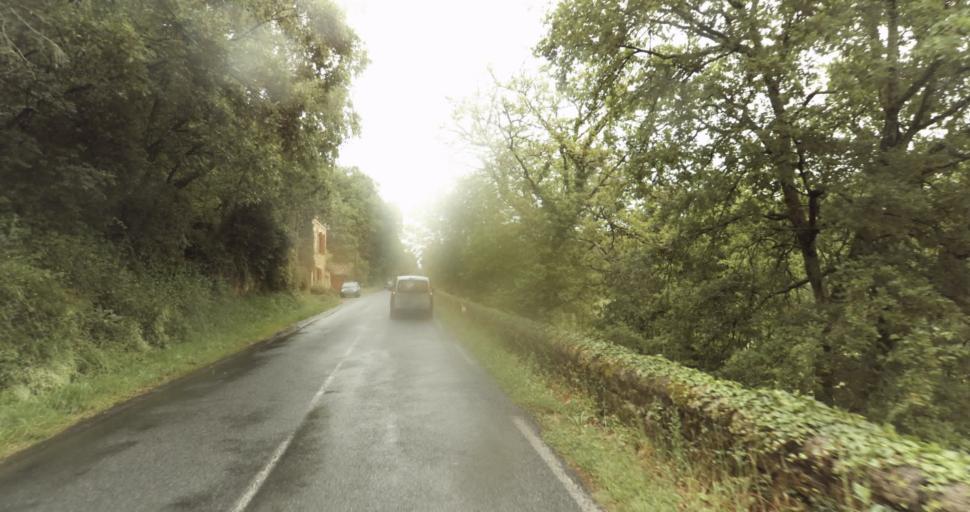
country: FR
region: Aquitaine
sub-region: Departement de la Dordogne
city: Beaumont-du-Perigord
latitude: 44.7732
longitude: 0.8124
